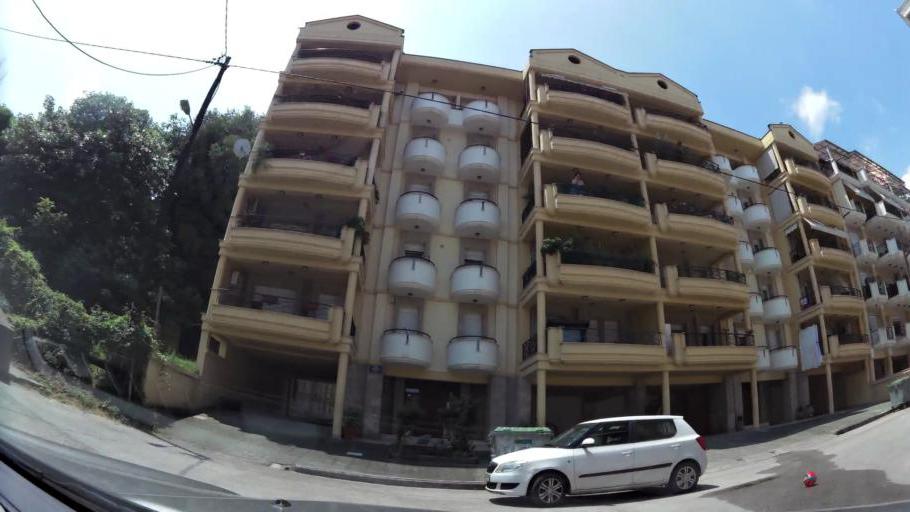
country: GR
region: Central Macedonia
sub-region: Nomos Imathias
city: Veroia
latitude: 40.5194
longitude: 22.1962
